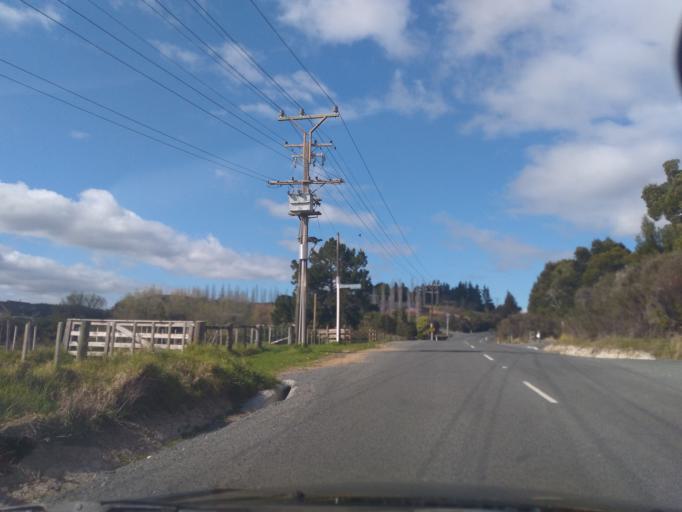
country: NZ
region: Northland
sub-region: Whangarei
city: Whangarei
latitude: -35.7040
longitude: 174.3535
